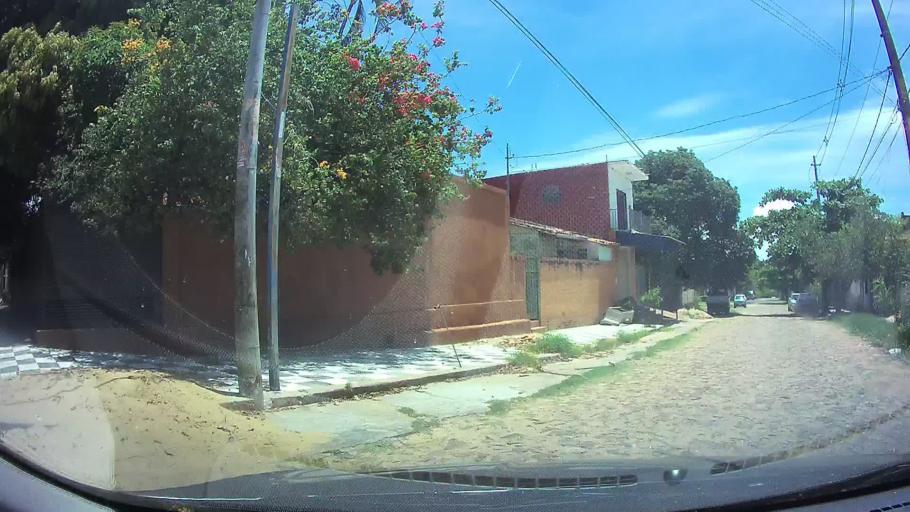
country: PY
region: Asuncion
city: Asuncion
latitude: -25.2722
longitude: -57.6003
